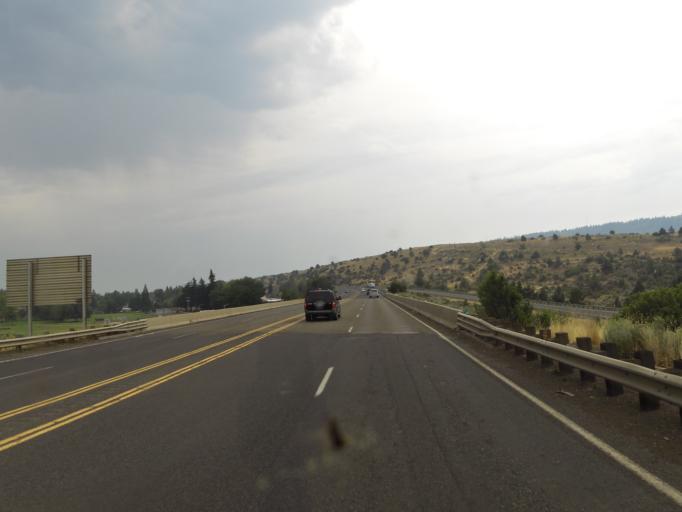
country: US
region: Oregon
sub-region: Klamath County
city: Klamath Falls
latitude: 42.2385
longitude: -121.7966
